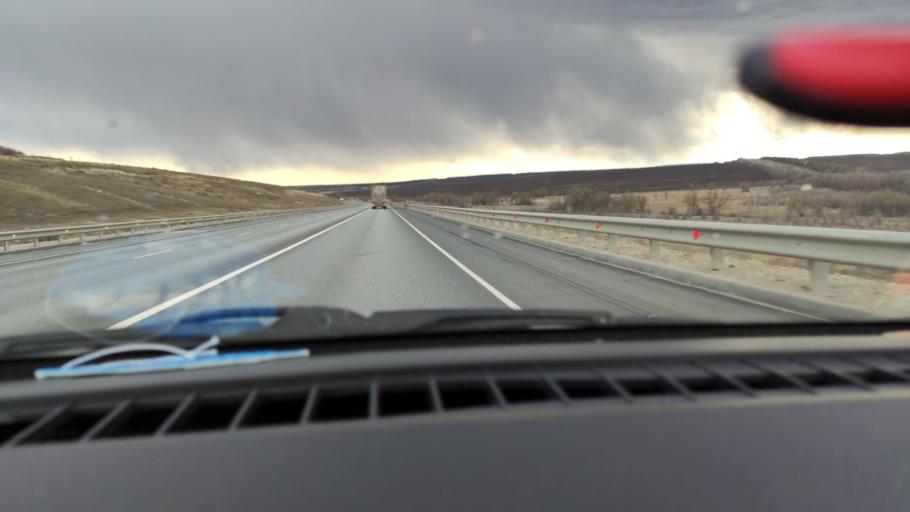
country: RU
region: Saratov
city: Yelshanka
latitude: 51.8725
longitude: 46.5042
